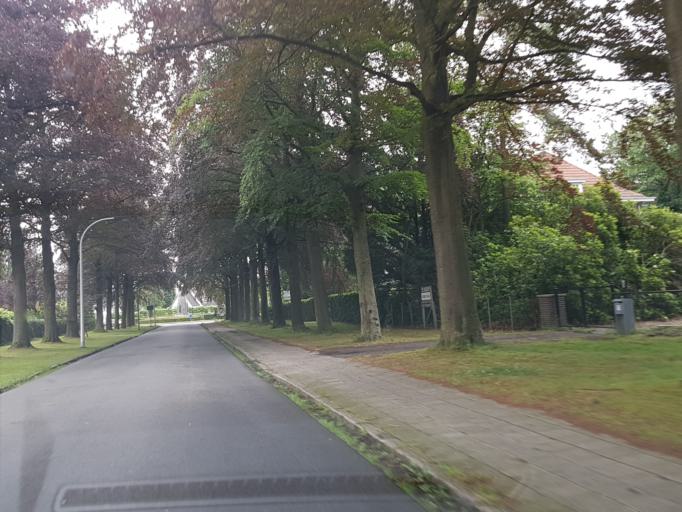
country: BE
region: Flanders
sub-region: Provincie Antwerpen
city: Brasschaat
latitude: 51.2891
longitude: 4.4768
